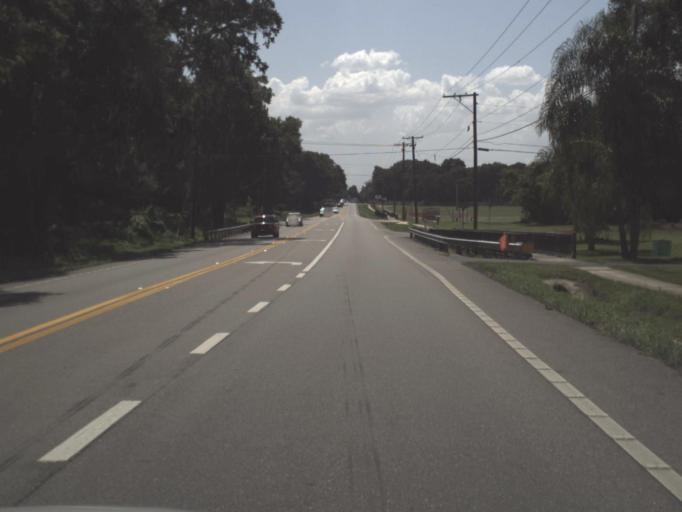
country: US
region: Florida
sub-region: Hillsborough County
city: Dover
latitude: 28.0211
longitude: -82.2227
